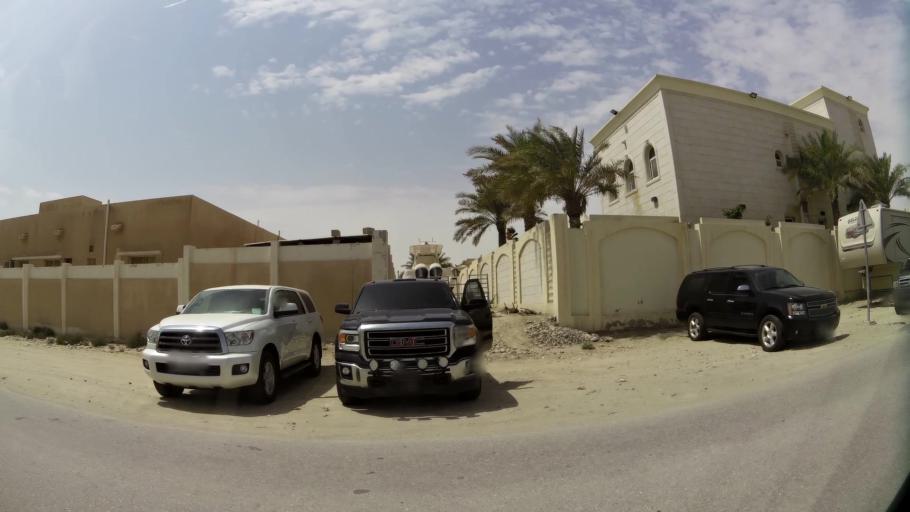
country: QA
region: Baladiyat ar Rayyan
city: Ar Rayyan
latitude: 25.3529
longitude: 51.4764
